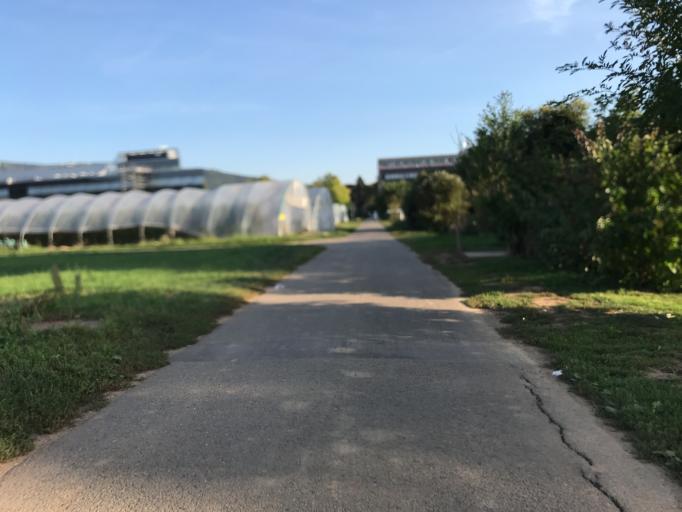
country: DE
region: Baden-Wuerttemberg
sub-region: Karlsruhe Region
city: Heidelberg
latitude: 49.4245
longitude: 8.6755
